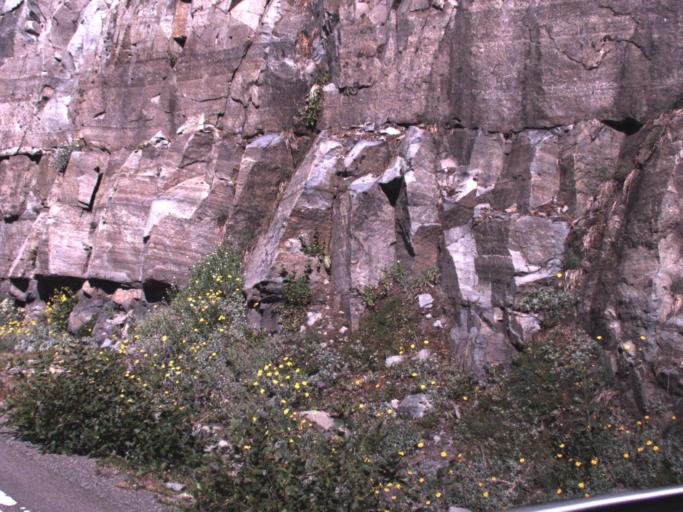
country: US
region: Washington
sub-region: King County
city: Enumclaw
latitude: 46.8693
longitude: -121.5329
